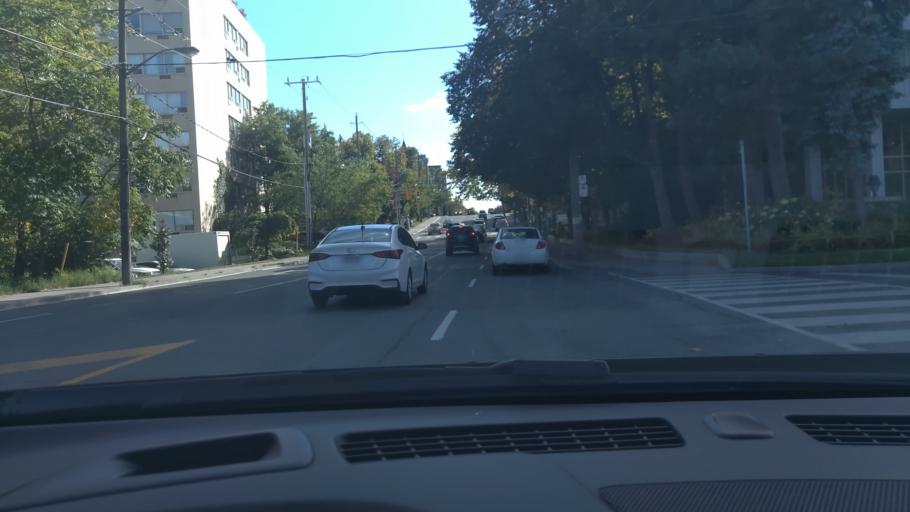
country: CA
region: Ontario
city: Toronto
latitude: 43.7088
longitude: -79.4273
